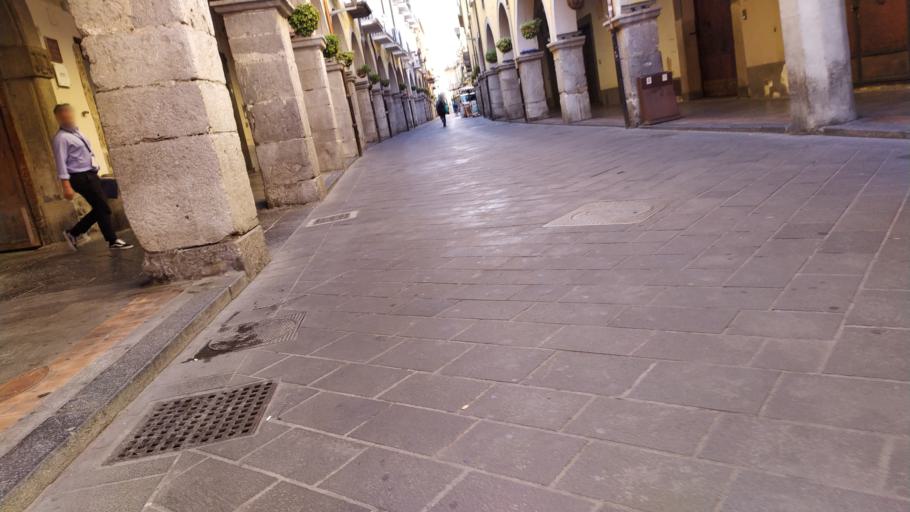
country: IT
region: Campania
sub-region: Provincia di Salerno
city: Cava De Tirreni
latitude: 40.6985
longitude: 14.7090
